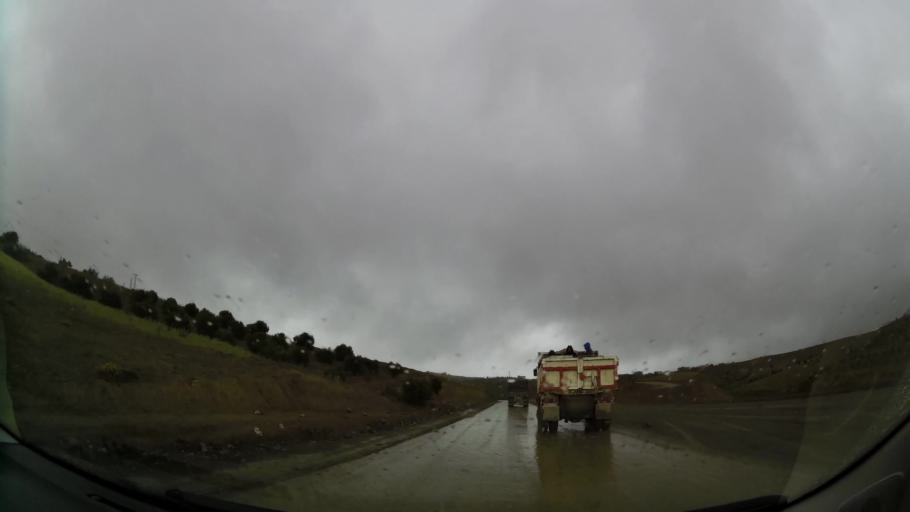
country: MA
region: Oriental
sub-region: Nador
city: Midar
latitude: 34.8890
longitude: -3.7561
